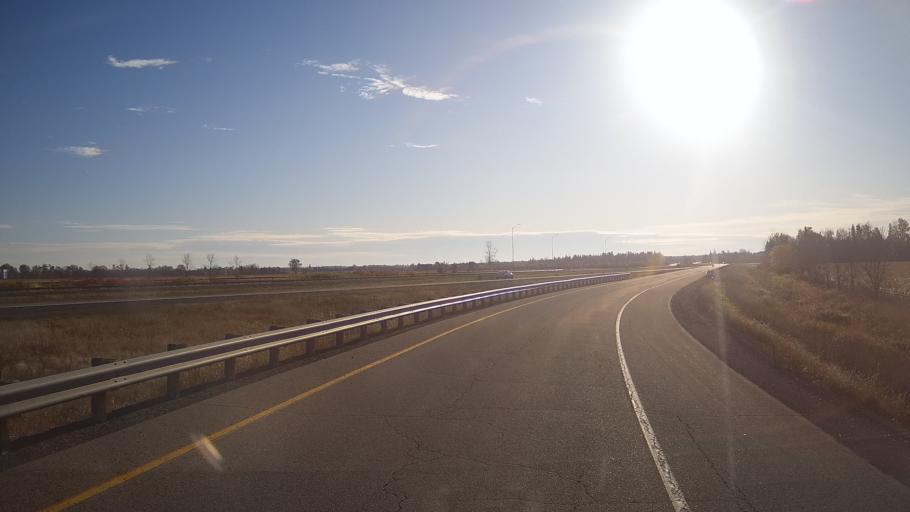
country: CA
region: Ontario
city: Arnprior
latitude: 45.3617
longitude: -76.2347
